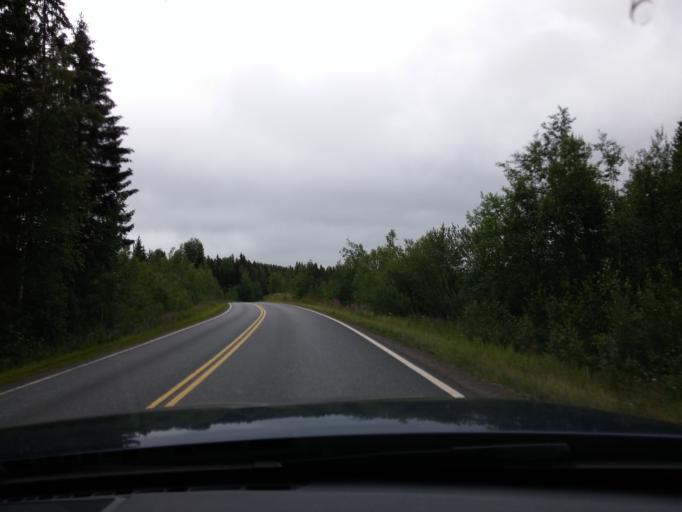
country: FI
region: Central Finland
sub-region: Joutsa
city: Luhanka
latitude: 61.8256
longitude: 25.9074
